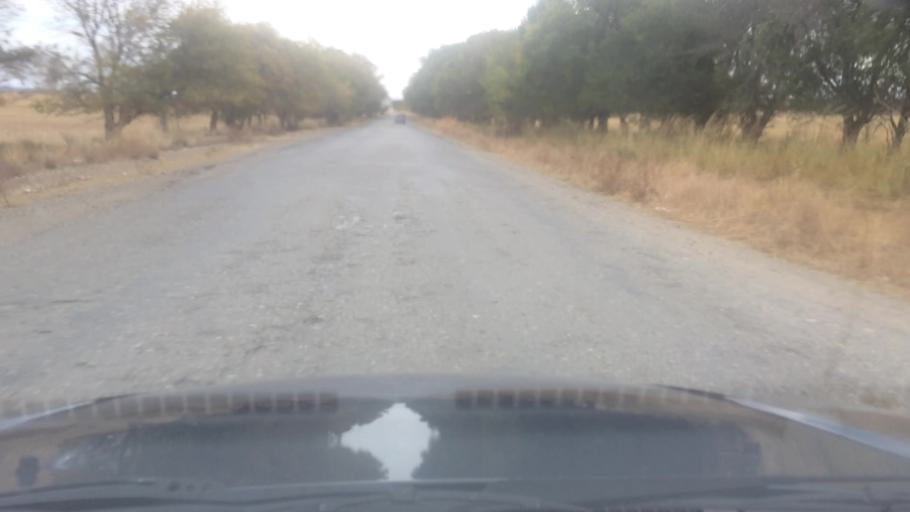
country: KG
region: Ysyk-Koel
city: Balykchy
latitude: 42.3096
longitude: 76.4611
